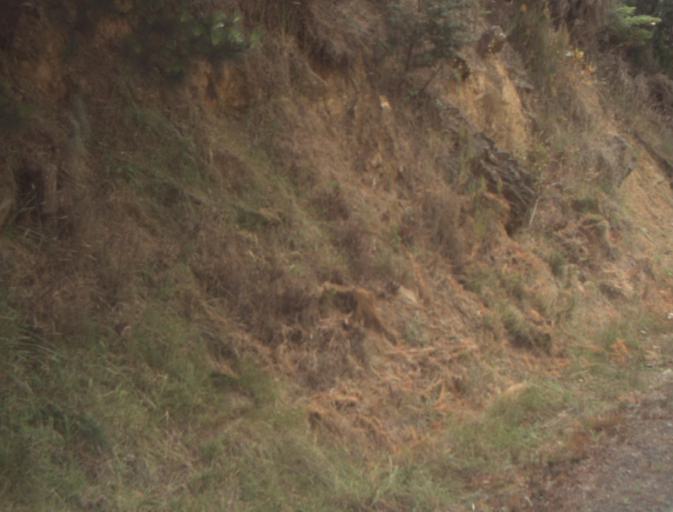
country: AU
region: Tasmania
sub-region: Launceston
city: Mayfield
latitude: -41.2710
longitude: 147.2149
